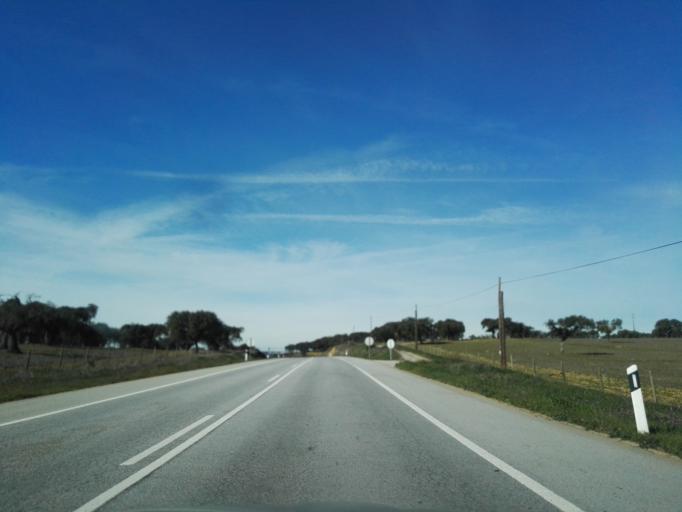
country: PT
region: Portalegre
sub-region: Portalegre
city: Alegrete
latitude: 39.1723
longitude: -7.3341
